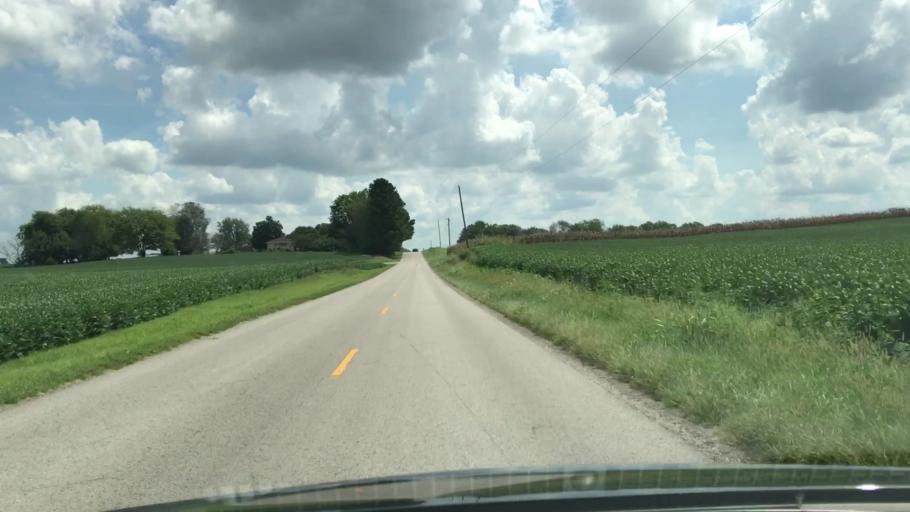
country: US
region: Kentucky
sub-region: Todd County
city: Guthrie
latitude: 36.7126
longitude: -87.0587
